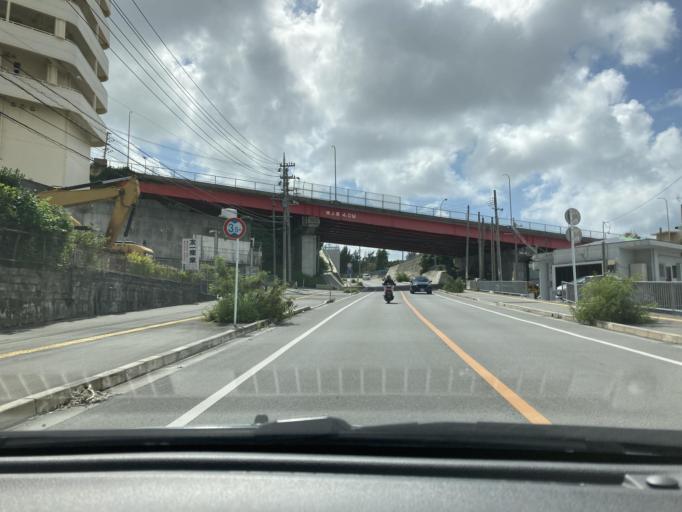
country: JP
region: Okinawa
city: Ginowan
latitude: 26.2607
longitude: 127.7277
